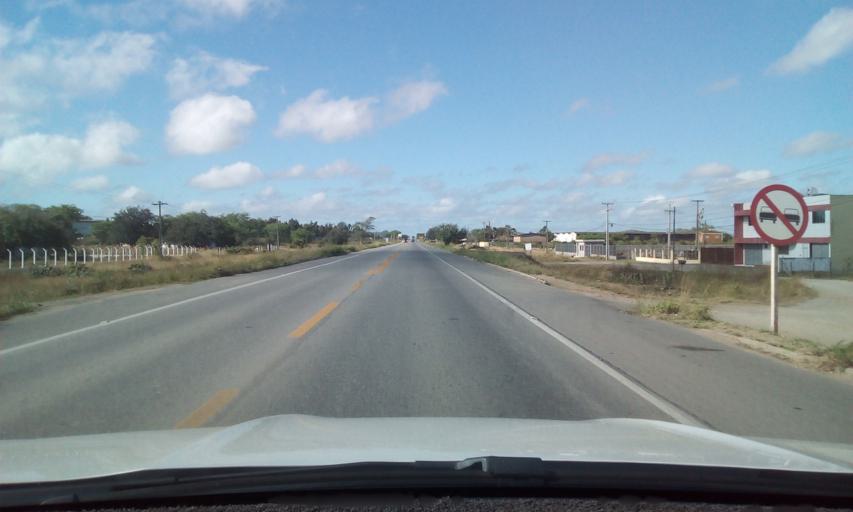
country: BR
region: Paraiba
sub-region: Campina Grande
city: Campina Grande
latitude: -7.2969
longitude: -35.8915
